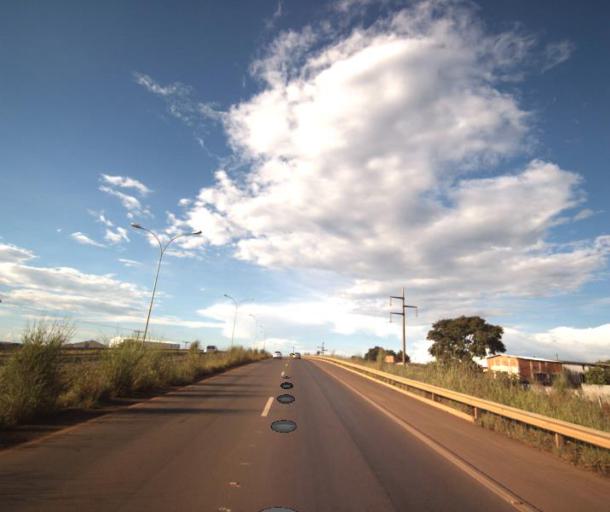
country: BR
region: Goias
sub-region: Anapolis
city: Anapolis
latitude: -16.3418
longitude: -48.9236
